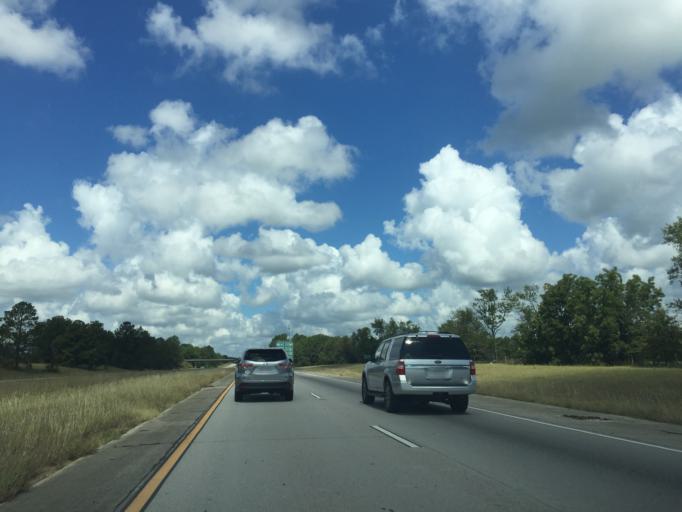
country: US
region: Georgia
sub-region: Candler County
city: Metter
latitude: 32.3516
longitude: -81.9796
